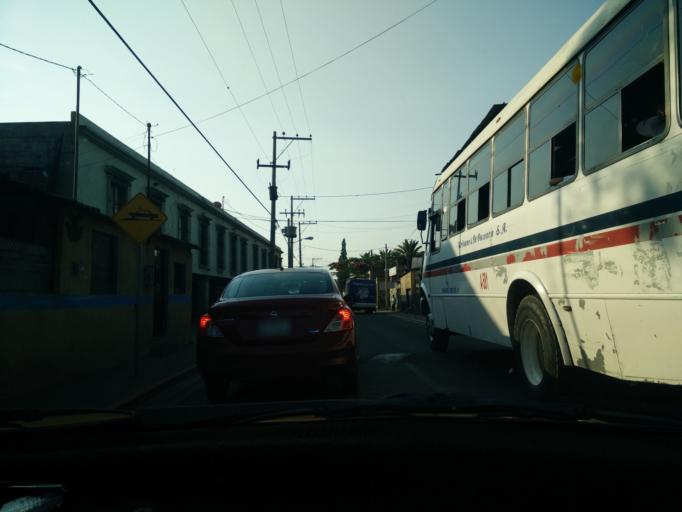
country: MX
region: Oaxaca
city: Oaxaca de Juarez
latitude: 17.0719
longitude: -96.7371
